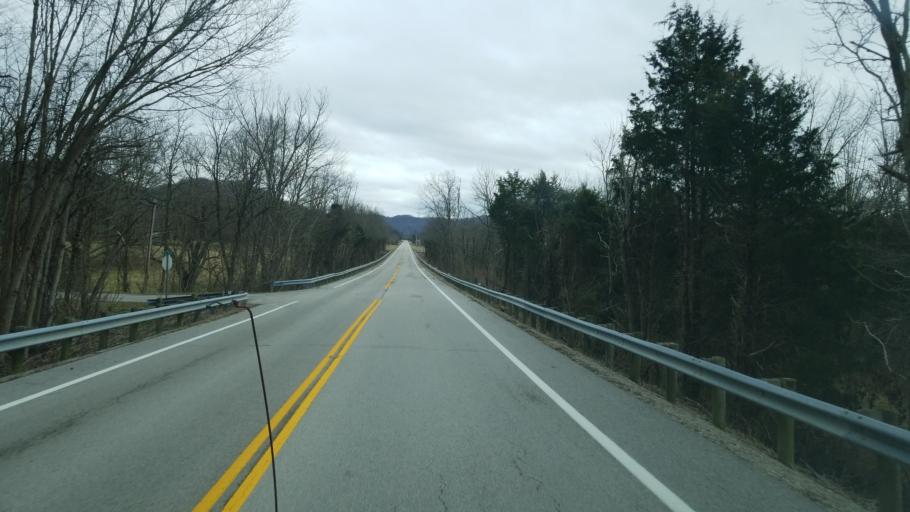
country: US
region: Ohio
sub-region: Adams County
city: West Union
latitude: 38.6826
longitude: -83.4572
